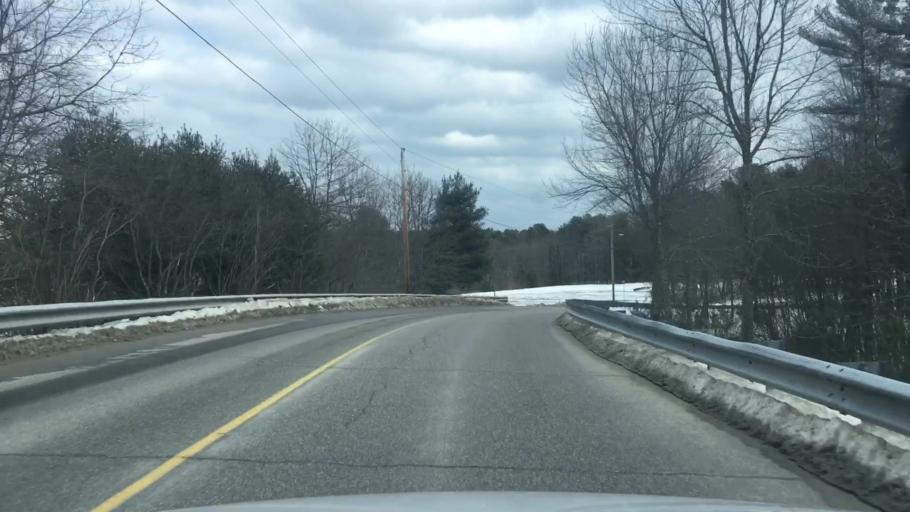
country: US
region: Maine
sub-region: York County
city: Arundel
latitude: 43.4063
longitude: -70.5082
